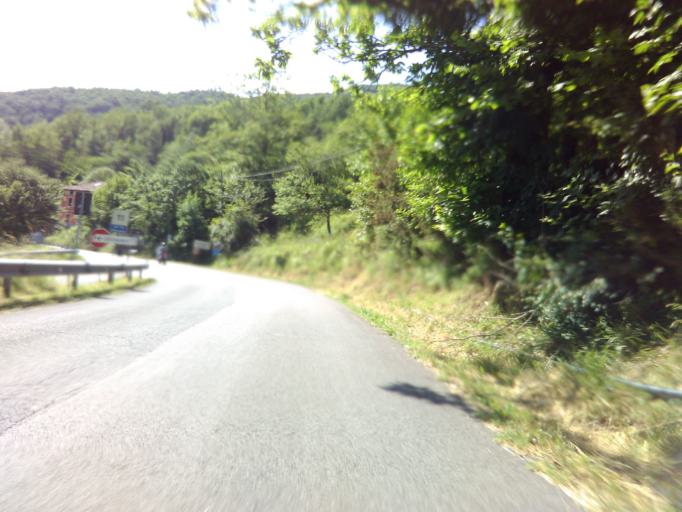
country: IT
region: Tuscany
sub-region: Provincia di Massa-Carrara
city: Licciana Nardi
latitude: 44.2841
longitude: 10.0741
